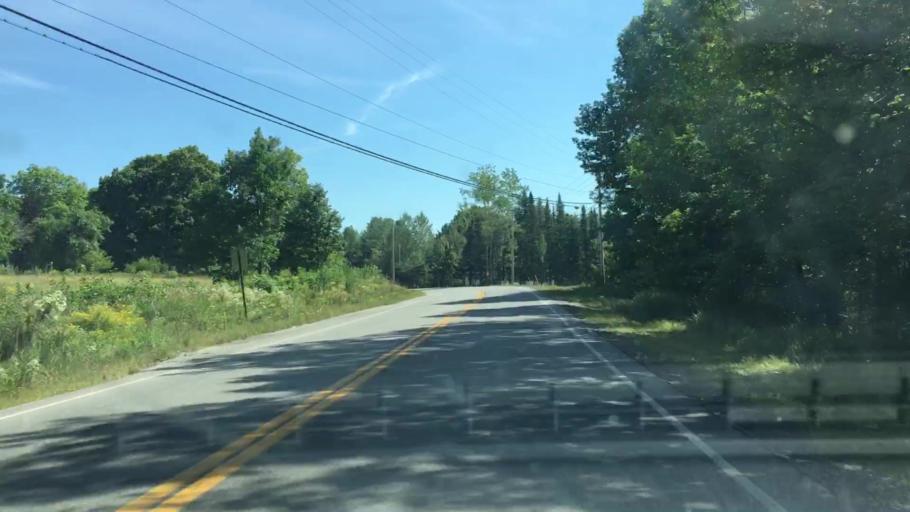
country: US
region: Maine
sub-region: Piscataquis County
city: Milo
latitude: 45.1895
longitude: -68.8964
